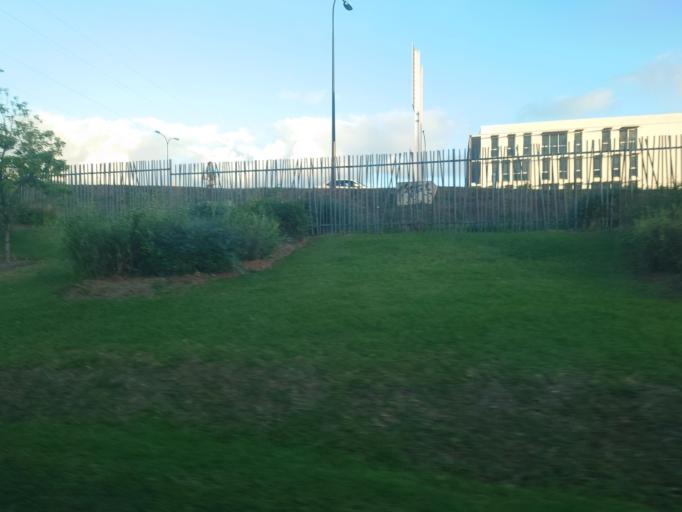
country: NC
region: South Province
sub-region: Dumbea
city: Dumbea
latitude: -22.2046
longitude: 166.4525
